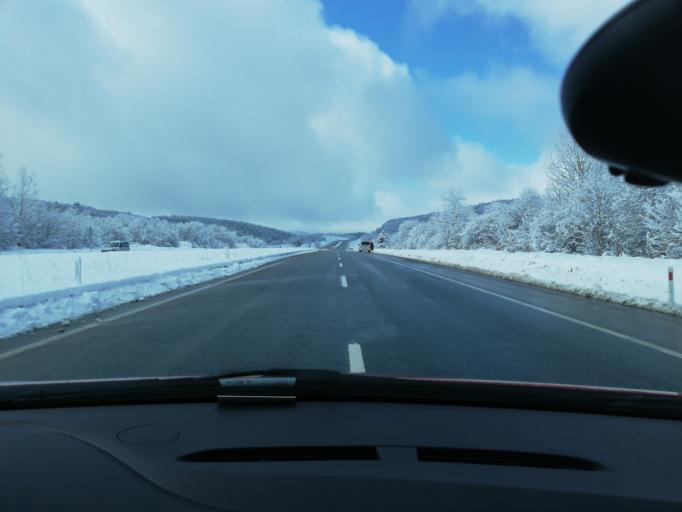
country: TR
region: Kastamonu
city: Kuzyaka
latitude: 41.3313
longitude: 33.6203
